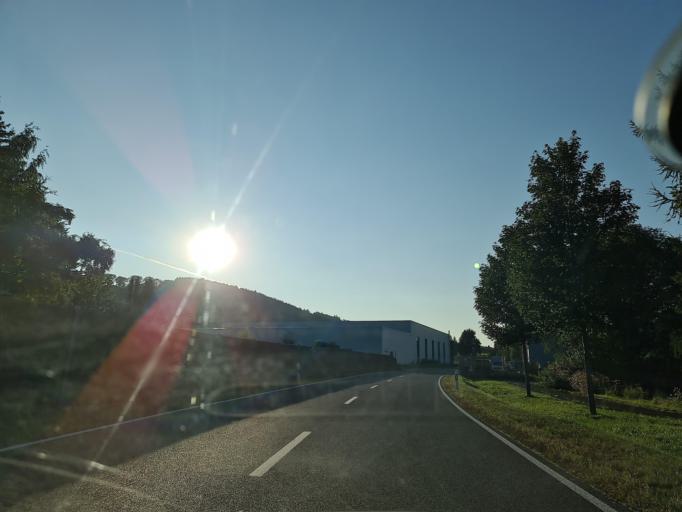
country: DE
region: Saxony
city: Olbernhau
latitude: 50.6498
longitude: 13.3540
